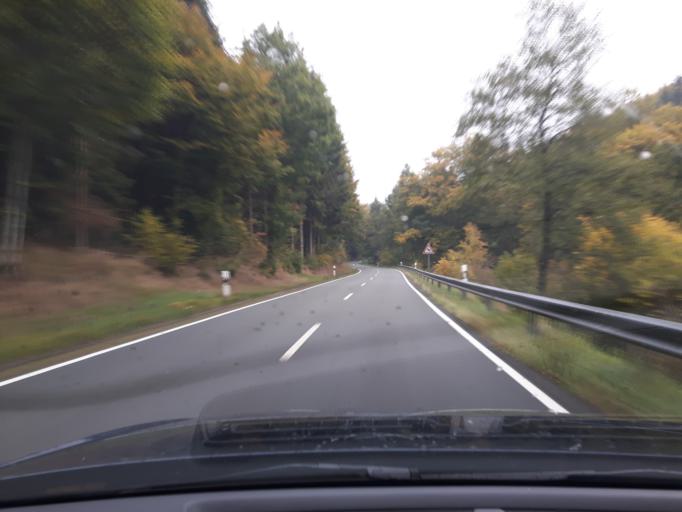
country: DE
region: North Rhine-Westphalia
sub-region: Regierungsbezirk Arnsberg
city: Bad Laasphe
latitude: 50.9614
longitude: 8.3884
